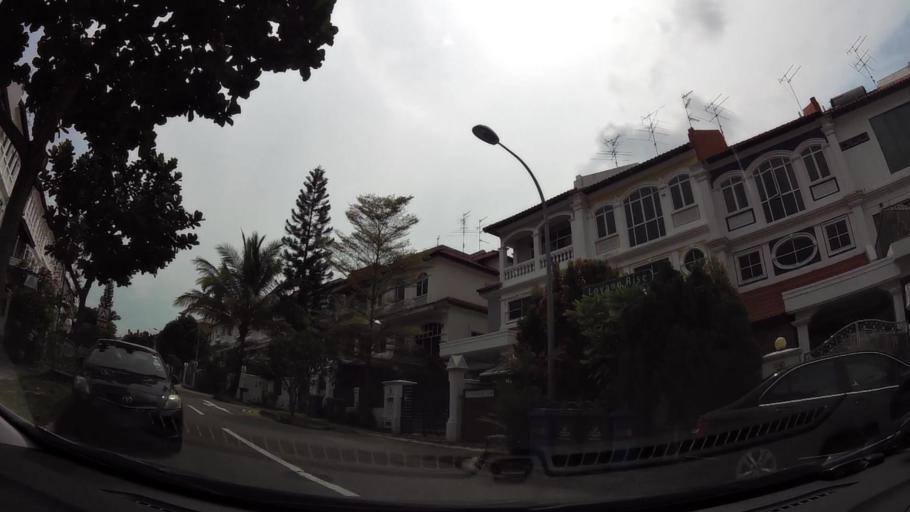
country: SG
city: Singapore
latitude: 1.3620
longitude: 103.9638
